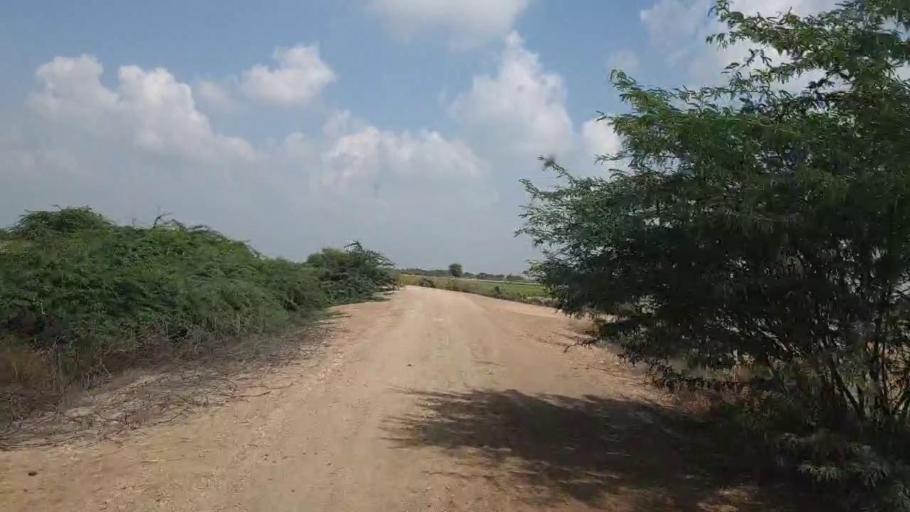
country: PK
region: Sindh
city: Badin
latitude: 24.4928
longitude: 68.6553
